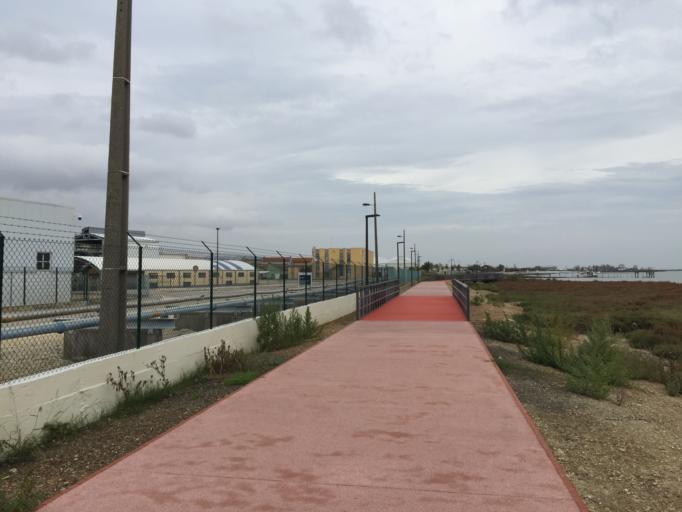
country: PT
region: Lisbon
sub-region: Vila Franca de Xira
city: Povoa de Santa Iria
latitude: 38.8546
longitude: -9.0640
